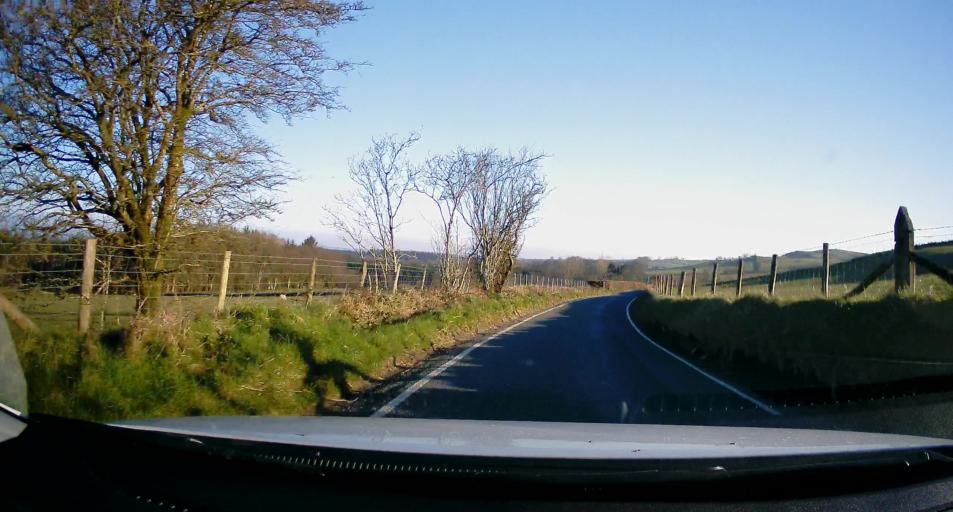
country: GB
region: Wales
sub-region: County of Ceredigion
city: Lledrod
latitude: 52.2607
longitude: -4.0748
